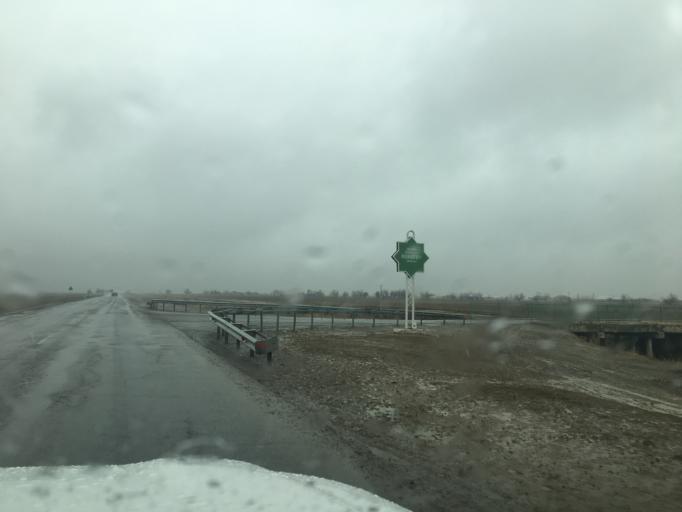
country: TM
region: Mary
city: Yoloeten
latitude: 37.3785
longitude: 62.1994
